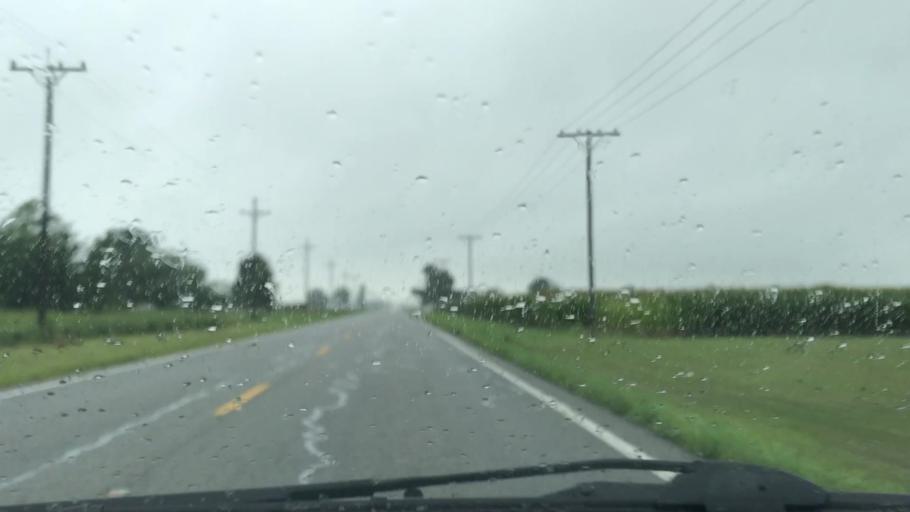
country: US
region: Indiana
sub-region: Hamilton County
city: Sheridan
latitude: 40.1284
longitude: -86.3078
